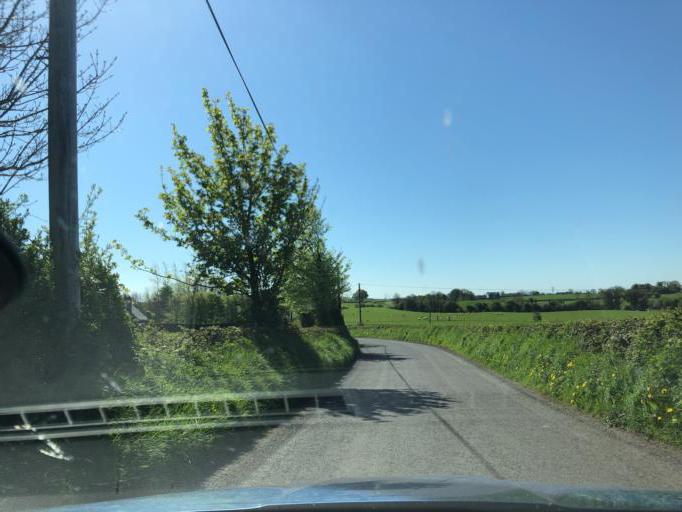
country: IE
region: Connaught
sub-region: County Galway
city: Portumna
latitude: 53.1512
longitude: -8.2932
